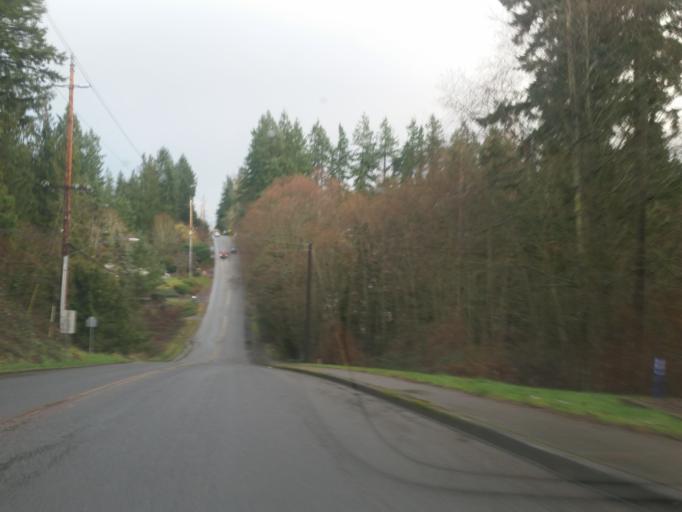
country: US
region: Washington
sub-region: Snohomish County
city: Brier
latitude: 47.7918
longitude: -122.2849
